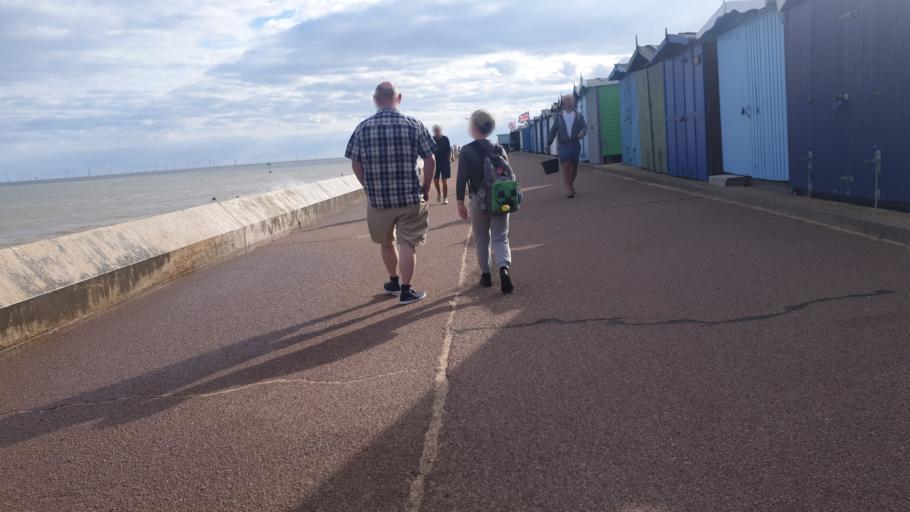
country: GB
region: England
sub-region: Essex
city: Frinton-on-Sea
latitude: 51.8246
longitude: 1.2433
